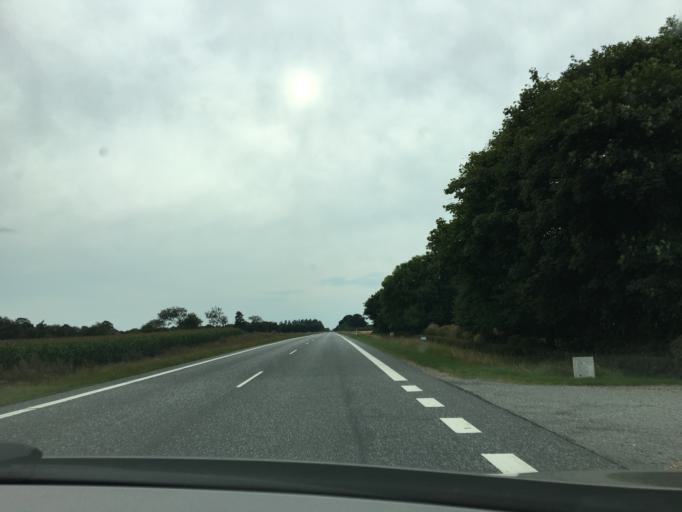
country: DK
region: Central Jutland
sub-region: Ringkobing-Skjern Kommune
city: Videbaek
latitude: 56.0881
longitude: 8.5471
